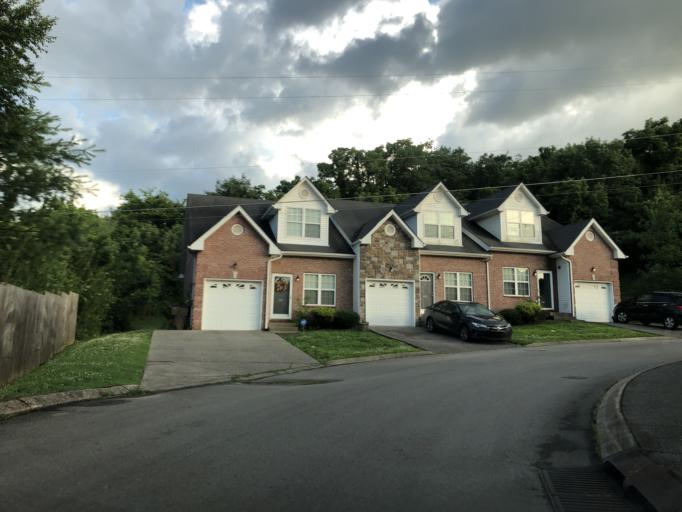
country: US
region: Tennessee
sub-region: Davidson County
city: Nashville
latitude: 36.1515
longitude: -86.7184
